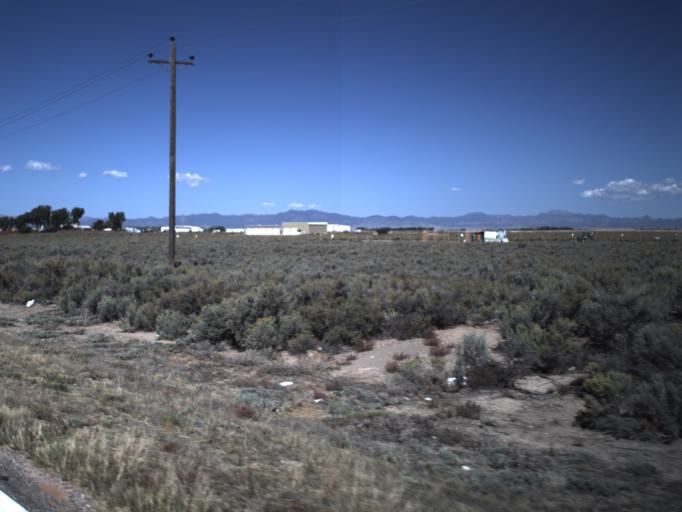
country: US
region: Utah
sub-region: Washington County
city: Enterprise
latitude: 37.7034
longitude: -113.6392
